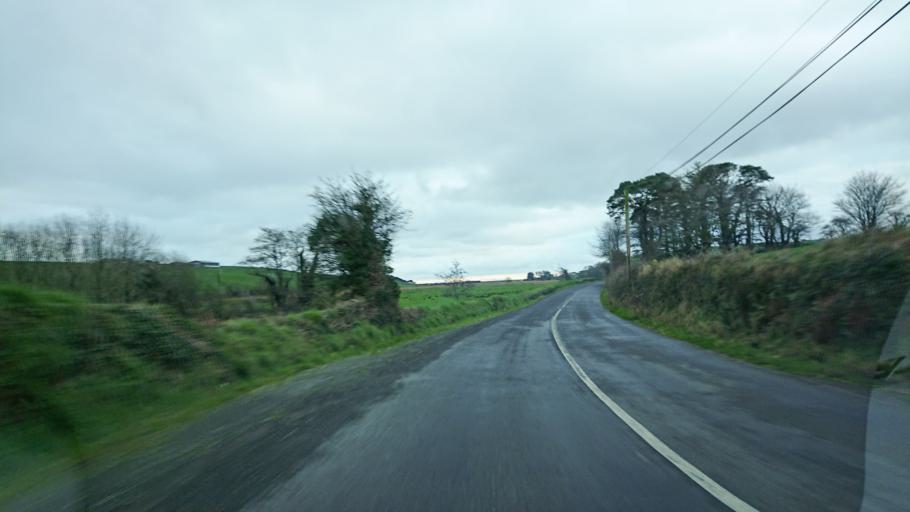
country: IE
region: Munster
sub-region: Waterford
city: Portlaw
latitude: 52.1519
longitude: -7.3802
